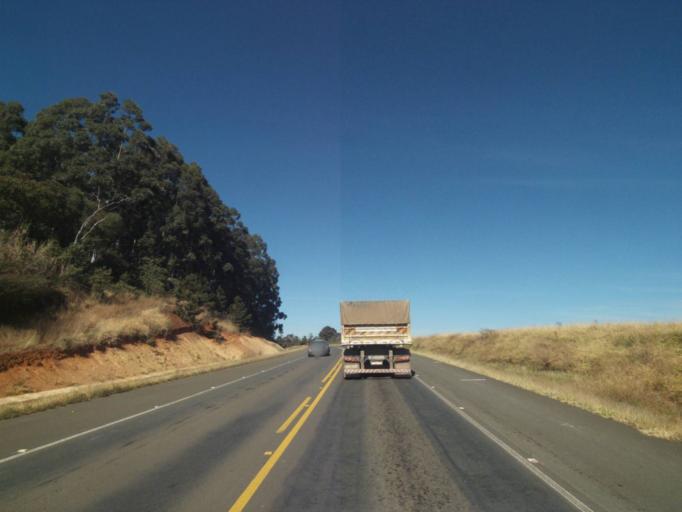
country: BR
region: Parana
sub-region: Tibagi
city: Tibagi
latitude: -24.7618
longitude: -50.4701
